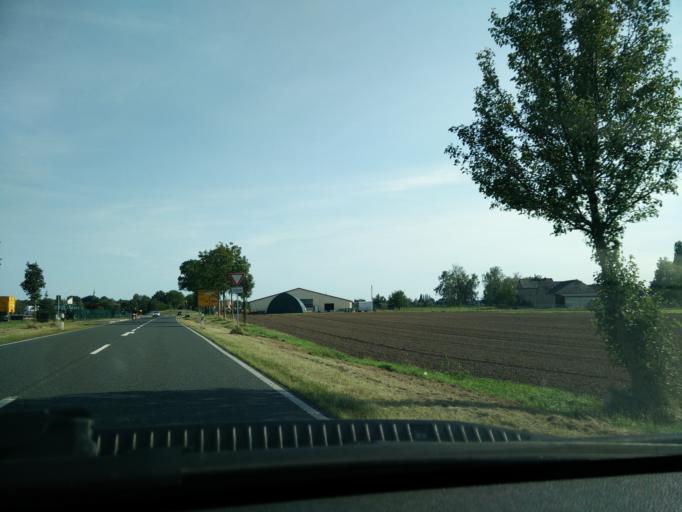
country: DE
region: Saxony
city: Bad Lausick
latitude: 51.1548
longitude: 12.6329
